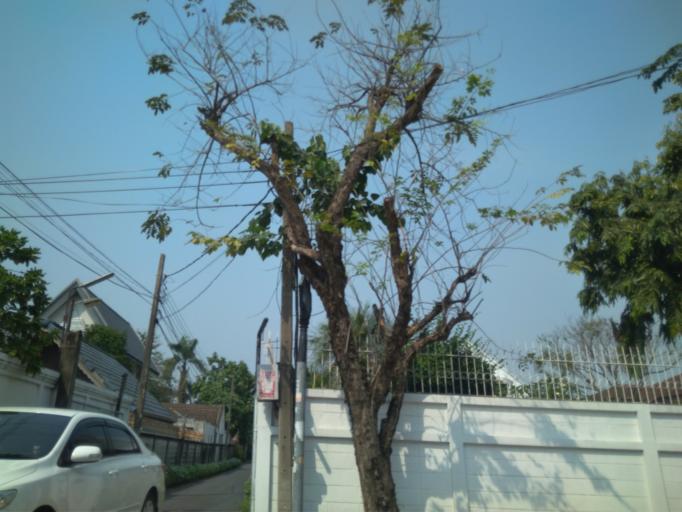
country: TH
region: Bangkok
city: Taling Chan
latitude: 13.7784
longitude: 100.4487
